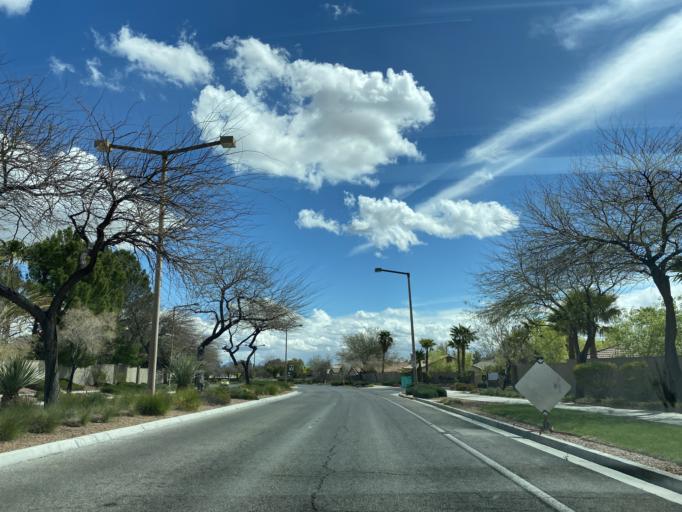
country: US
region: Nevada
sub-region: Clark County
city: Summerlin South
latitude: 36.1330
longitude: -115.3238
